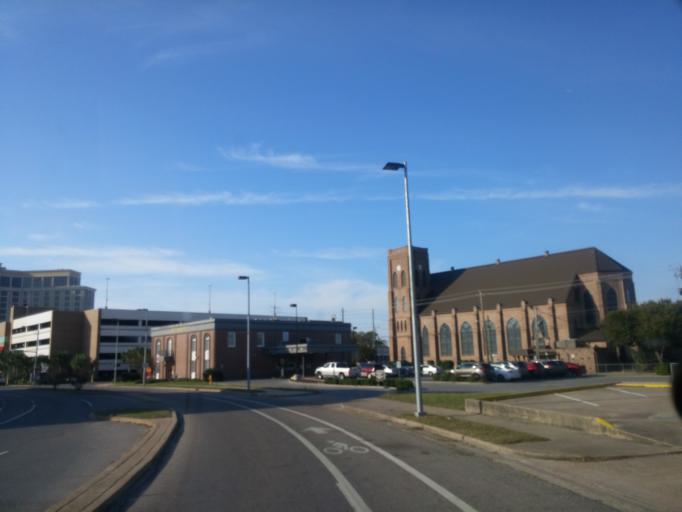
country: US
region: Mississippi
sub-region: Harrison County
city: Biloxi
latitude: 30.3977
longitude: -88.8903
